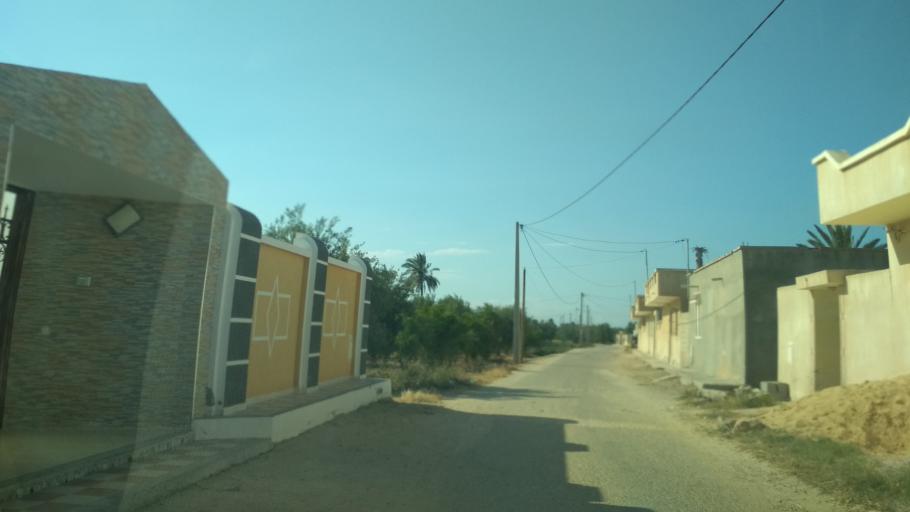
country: TN
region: Qabis
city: Gabes
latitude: 33.9504
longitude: 10.0608
